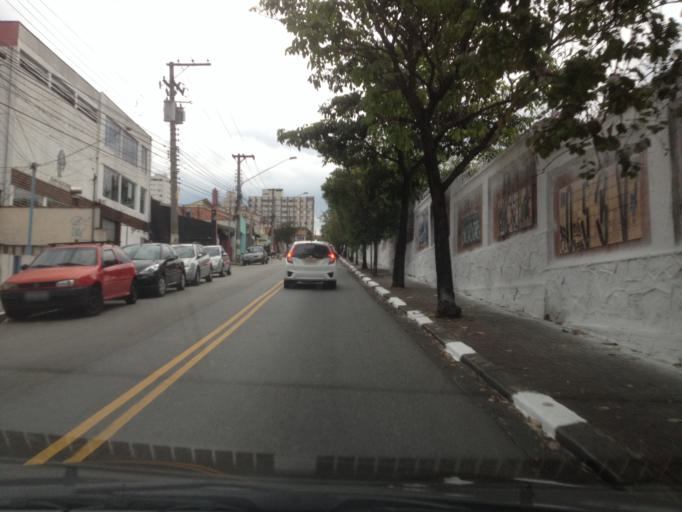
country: BR
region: Sao Paulo
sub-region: Sao Paulo
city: Sao Paulo
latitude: -23.5570
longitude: -46.6851
